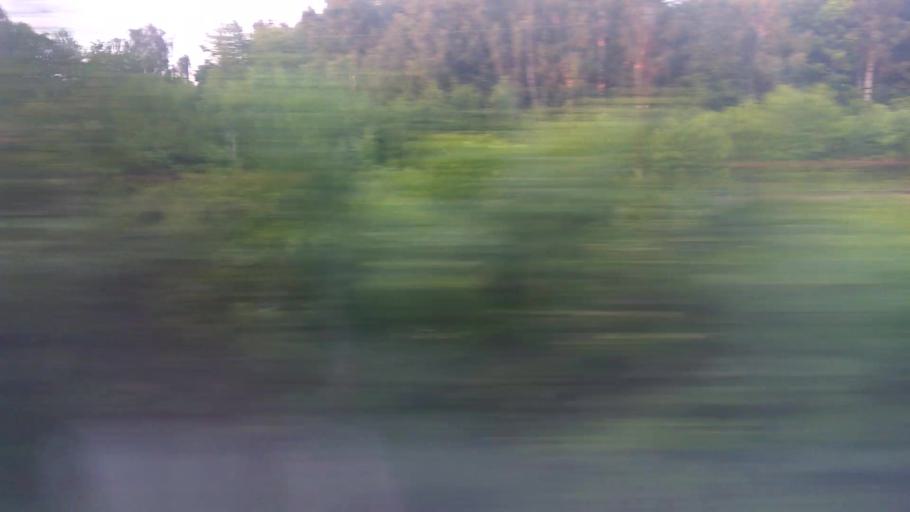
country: RU
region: Moskovskaya
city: Belyye Stolby
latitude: 55.3040
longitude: 37.8766
